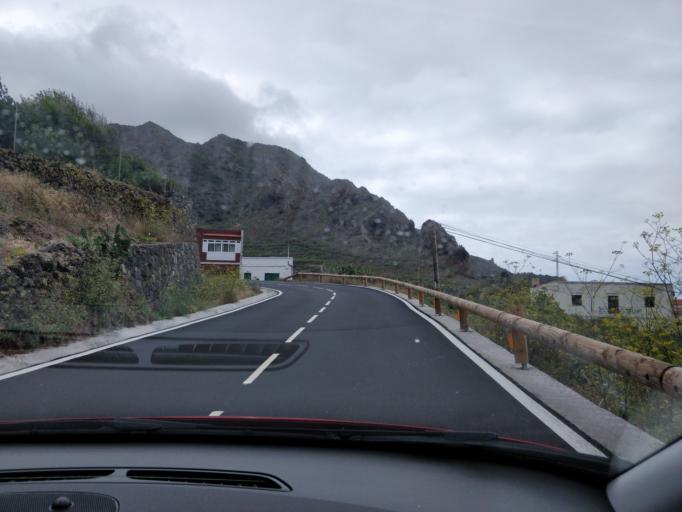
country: ES
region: Canary Islands
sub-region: Provincia de Santa Cruz de Tenerife
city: Tanque
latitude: 28.3459
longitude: -16.8455
